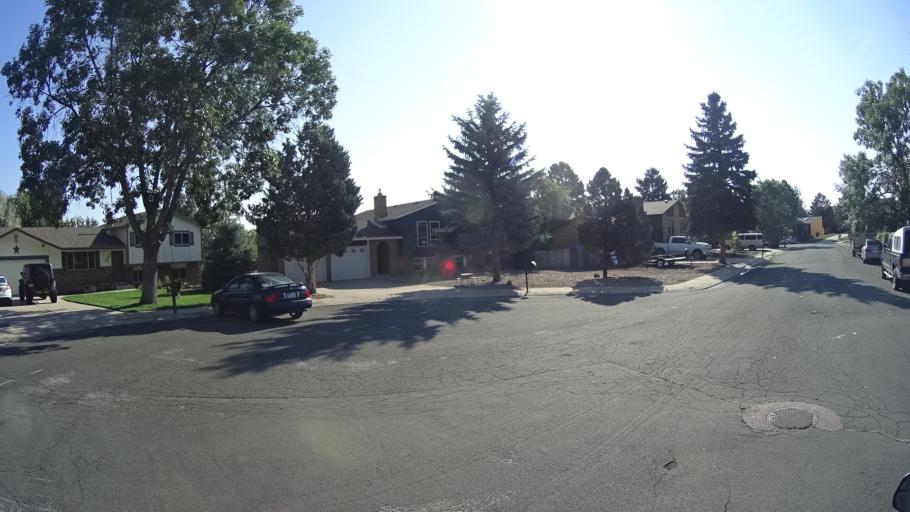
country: US
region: Colorado
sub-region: El Paso County
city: Colorado Springs
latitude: 38.8872
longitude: -104.8489
